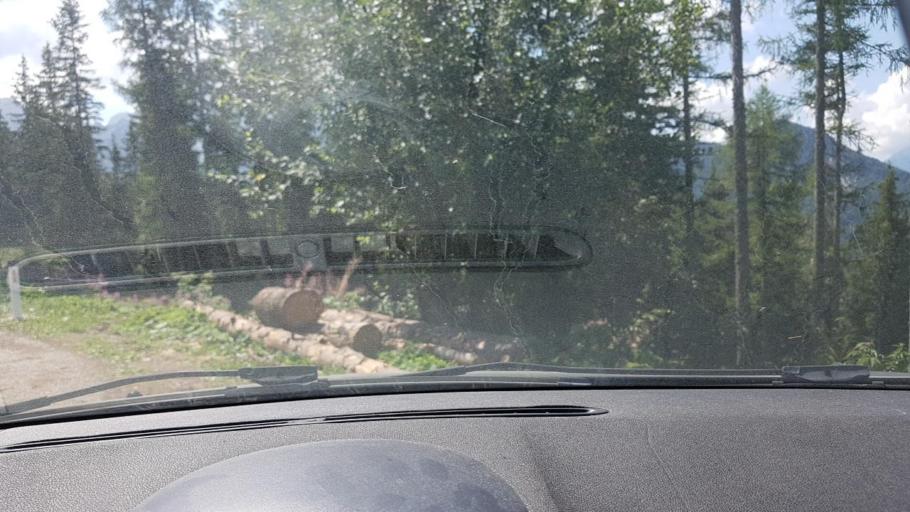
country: AT
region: Carinthia
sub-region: Politischer Bezirk Volkermarkt
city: Bad Eisenkappel
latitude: 46.4247
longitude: 14.5704
